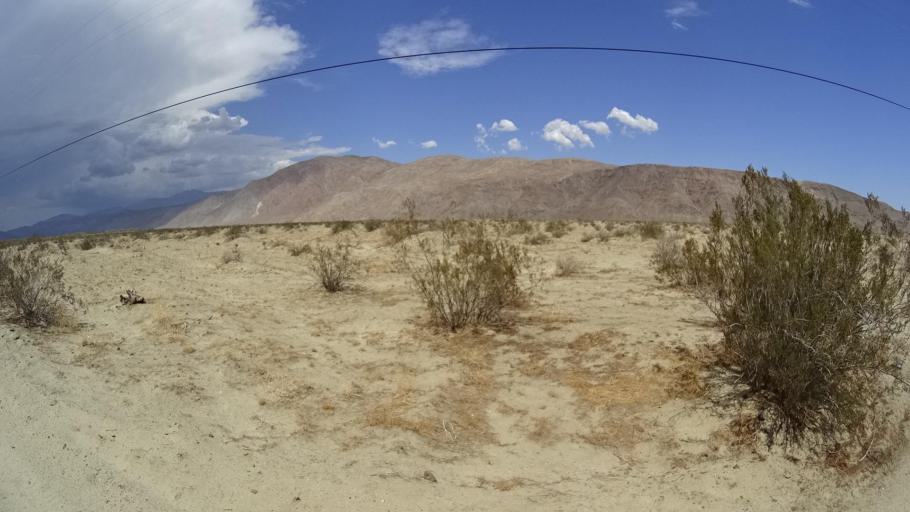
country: US
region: California
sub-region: San Diego County
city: Borrego Springs
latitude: 33.2963
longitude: -116.3331
